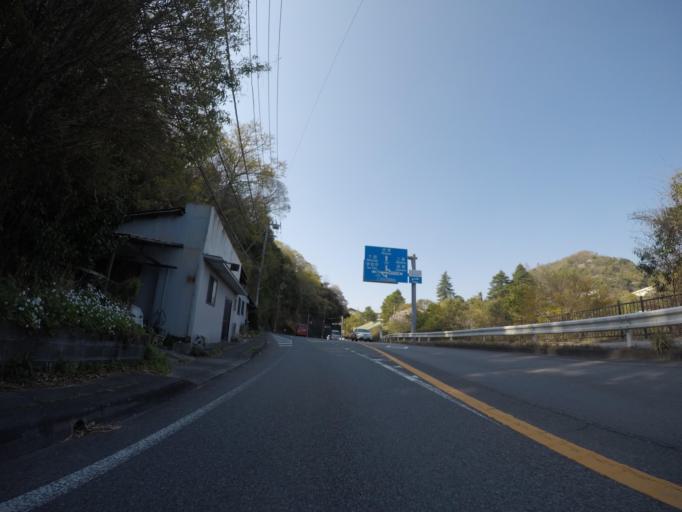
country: JP
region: Shizuoka
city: Mishima
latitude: 35.0404
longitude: 138.9238
